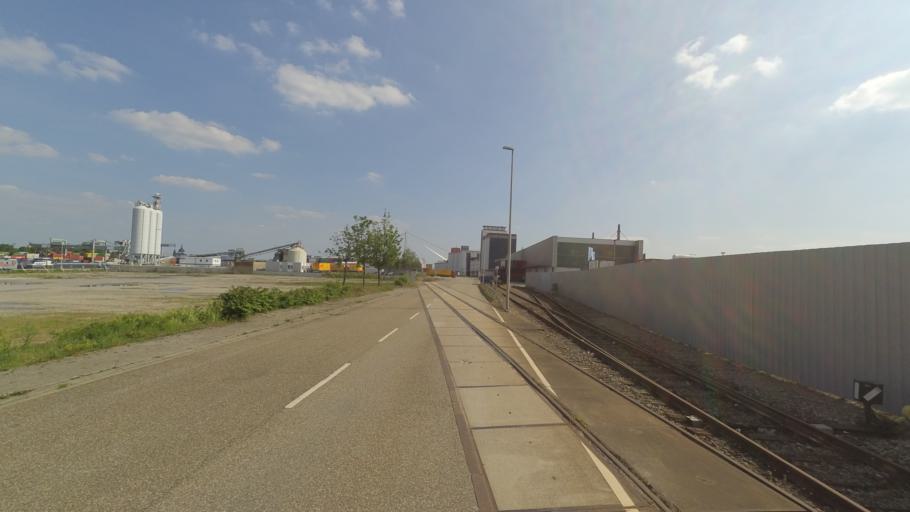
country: DE
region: Rheinland-Pfalz
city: Ludwigshafen am Rhein
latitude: 49.4972
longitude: 8.4438
